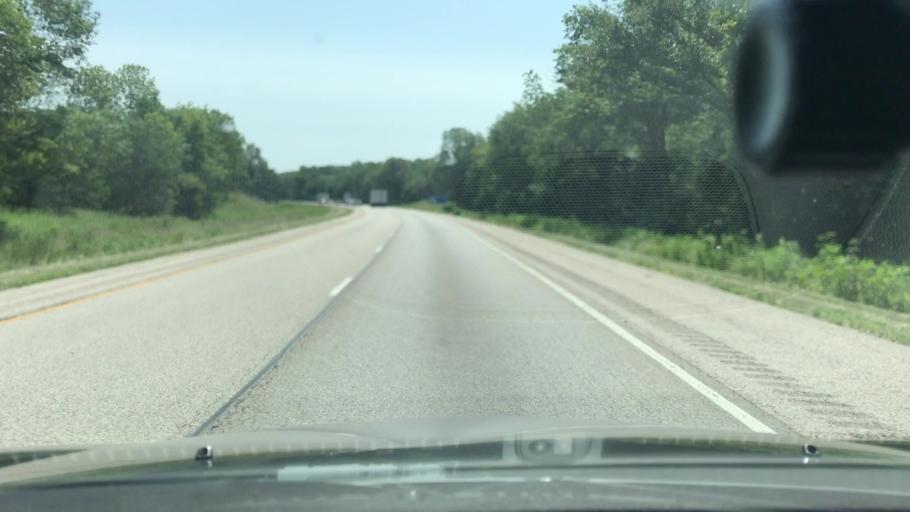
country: US
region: Illinois
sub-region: Washington County
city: Nashville
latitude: 38.4027
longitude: -89.4040
